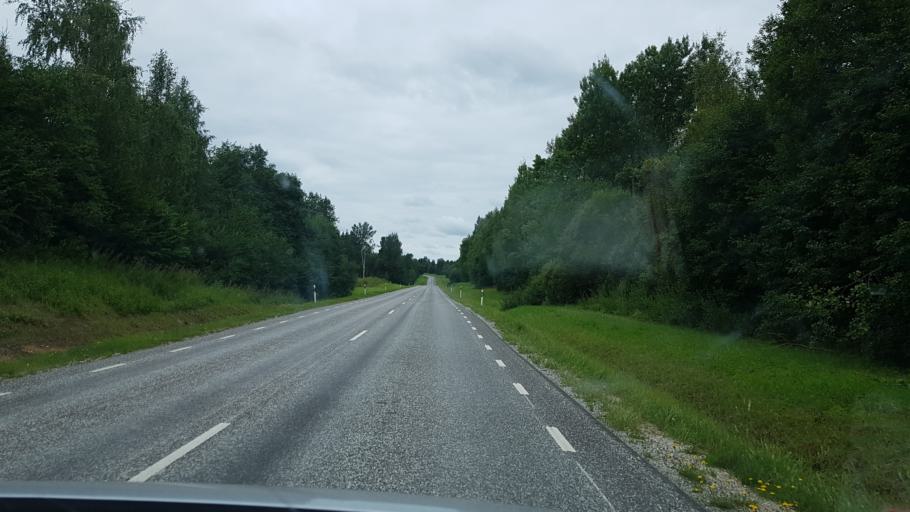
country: EE
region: Vorumaa
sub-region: Antsla vald
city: Vana-Antsla
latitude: 58.0049
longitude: 26.6975
